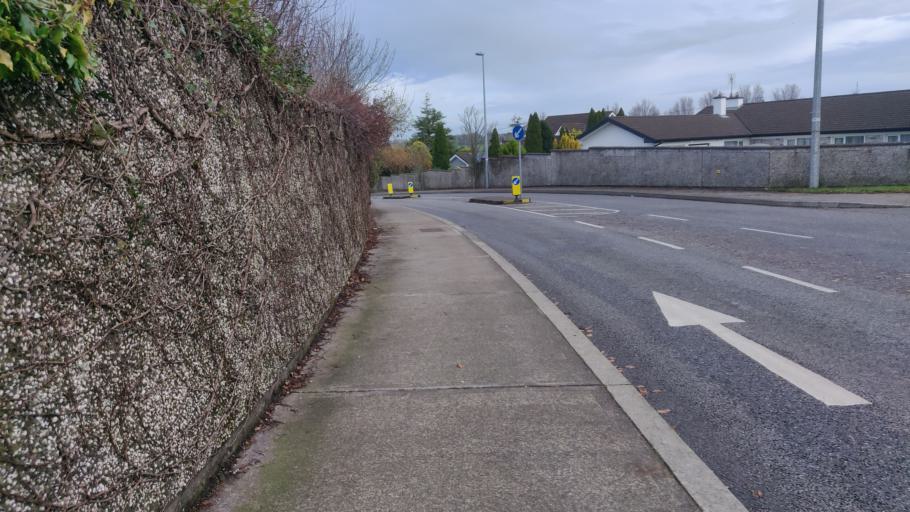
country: DE
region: North Rhine-Westphalia
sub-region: Regierungsbezirk Detmold
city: Guetersloh
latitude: 51.8630
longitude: 8.4013
